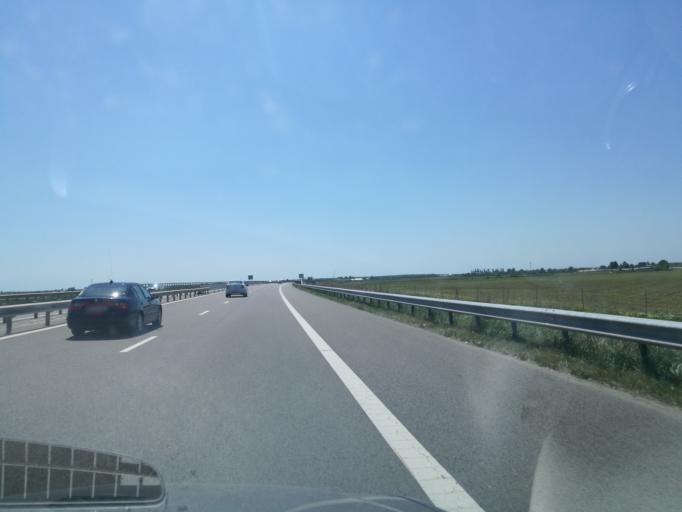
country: RO
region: Ilfov
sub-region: Comuna Gruiu
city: Gruiu
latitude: 44.7354
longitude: 26.2557
